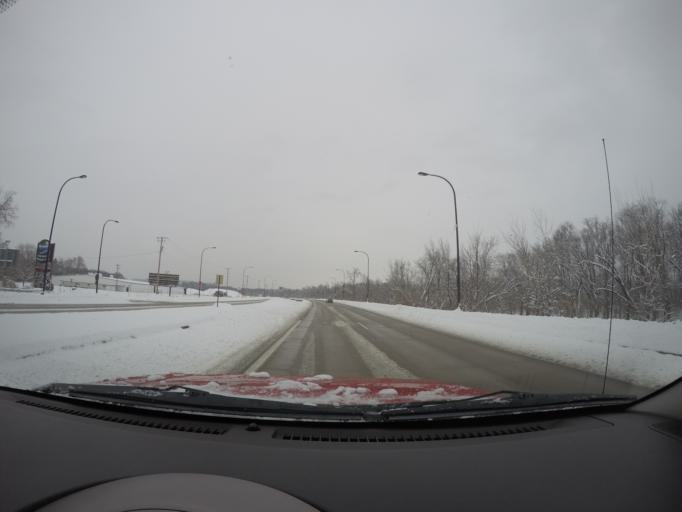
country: US
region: Wisconsin
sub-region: La Crosse County
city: La Crosse
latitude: 43.8129
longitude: -91.2653
